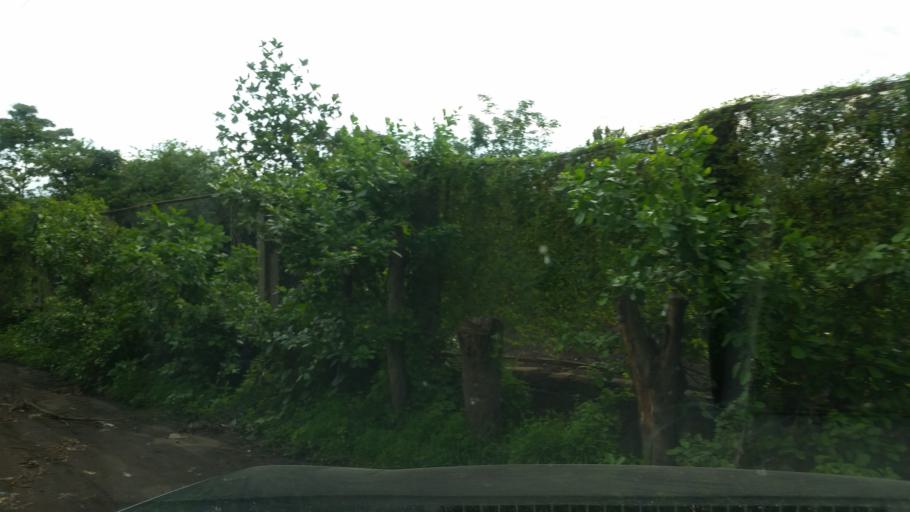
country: NI
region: Chinandega
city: Puerto Morazan
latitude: 12.7679
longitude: -87.1267
